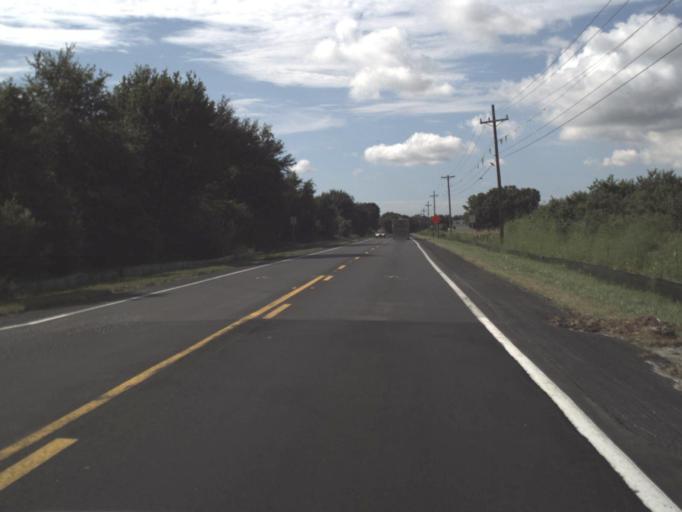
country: US
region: Florida
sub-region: Polk County
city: Combee Settlement
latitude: 28.1138
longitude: -81.9066
